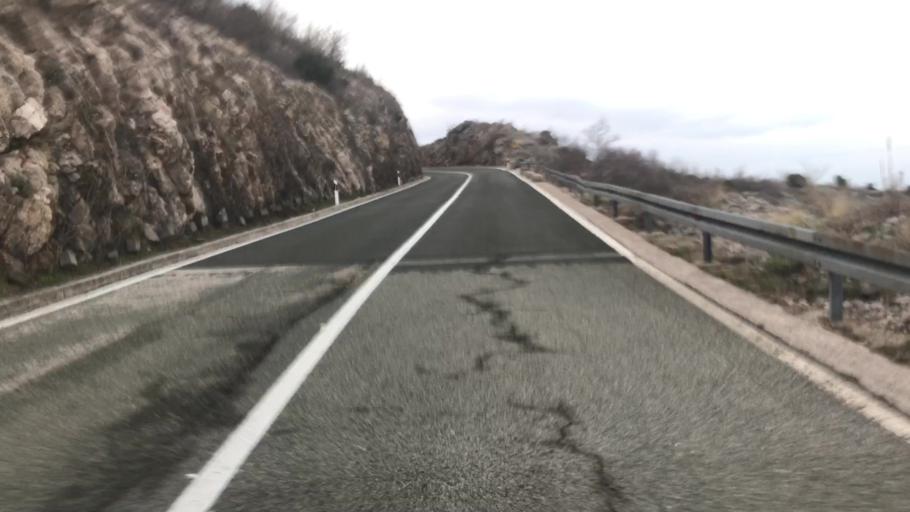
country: HR
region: Licko-Senjska
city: Novalja
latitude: 44.6652
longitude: 14.9458
